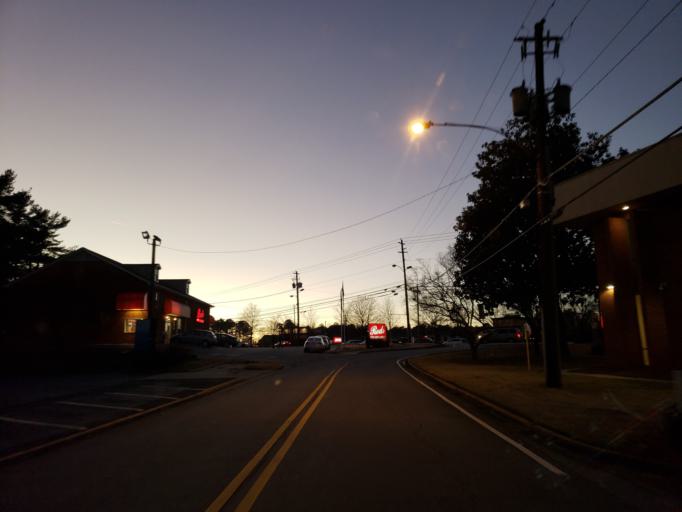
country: US
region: Georgia
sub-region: Fulton County
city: Alpharetta
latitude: 34.0684
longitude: -84.2989
